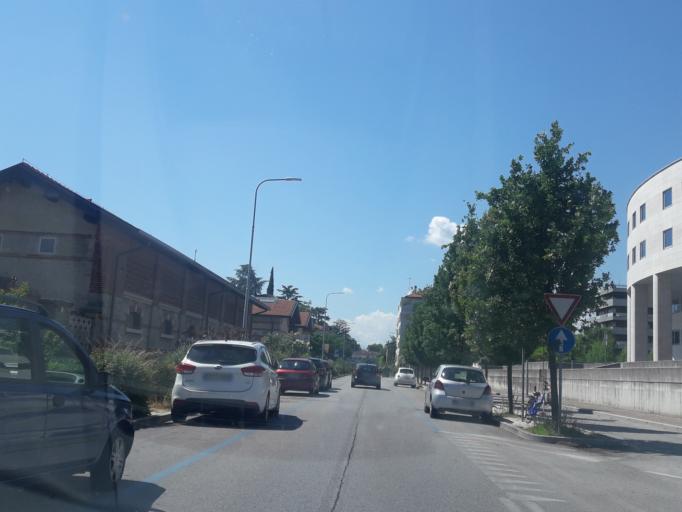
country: IT
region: Friuli Venezia Giulia
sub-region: Provincia di Udine
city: Udine
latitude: 46.0543
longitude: 13.2274
